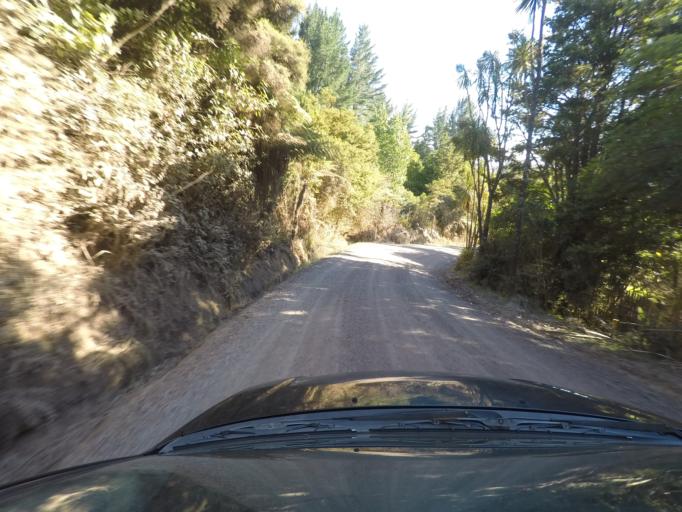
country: NZ
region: Northland
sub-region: Far North District
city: Paihia
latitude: -35.2550
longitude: 174.0710
